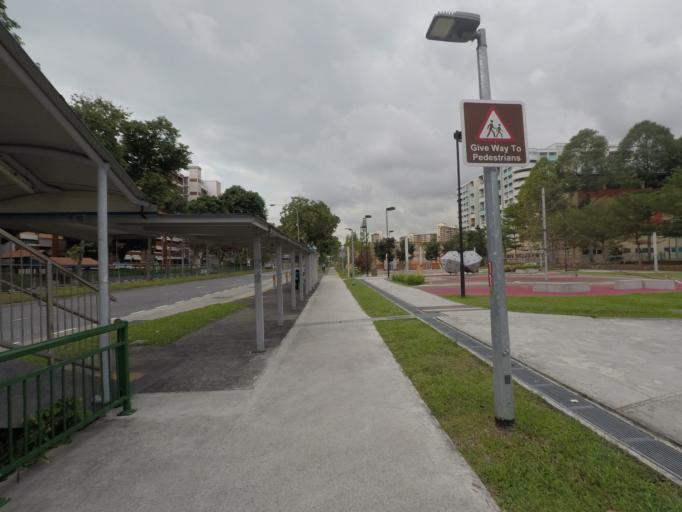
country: SG
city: Singapore
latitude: 1.3749
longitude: 103.8927
